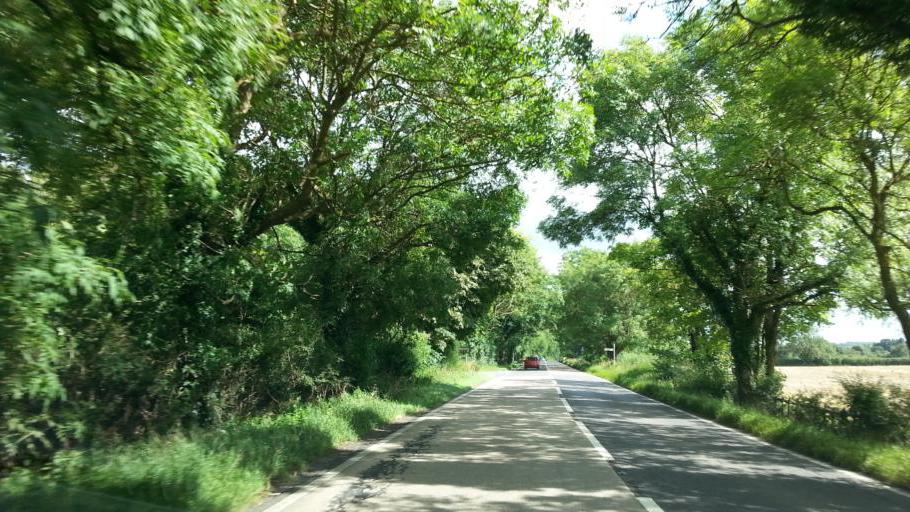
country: GB
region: England
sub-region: Nottinghamshire
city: Farnsfield
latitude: 53.1167
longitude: -0.9945
